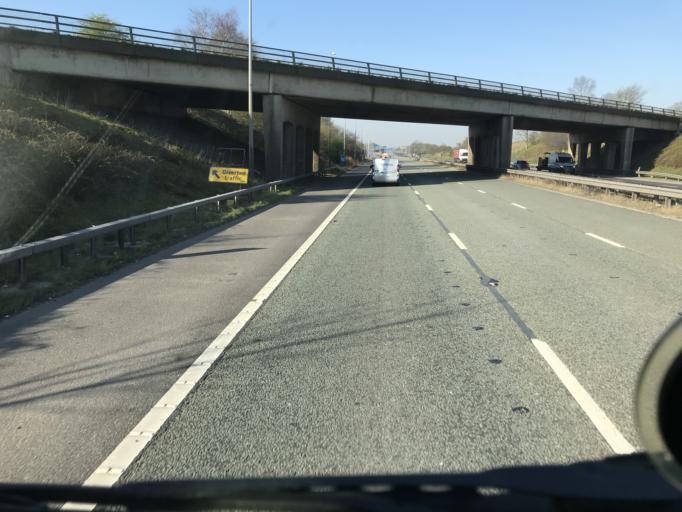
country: GB
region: England
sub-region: Warrington
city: Lymm
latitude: 53.3569
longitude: -2.4851
